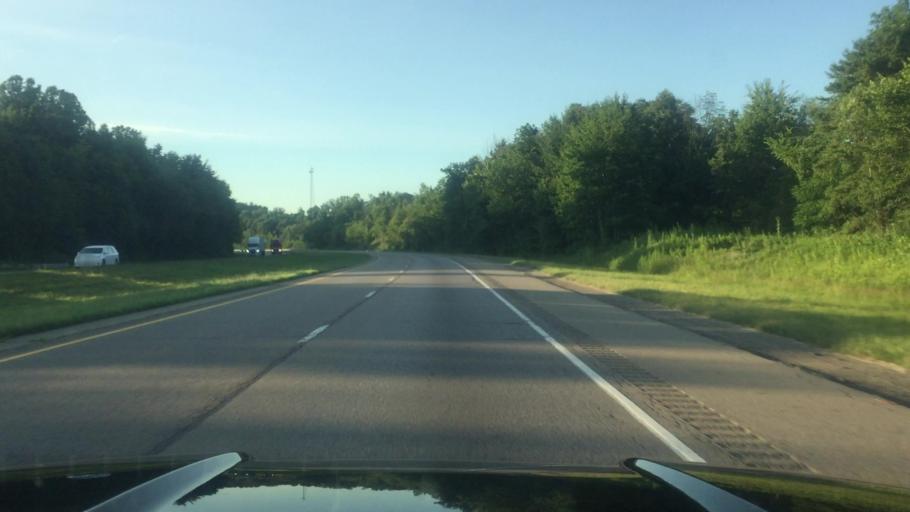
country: US
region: Ohio
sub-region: Tuscarawas County
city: Newcomerstown
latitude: 40.2156
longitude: -81.5530
